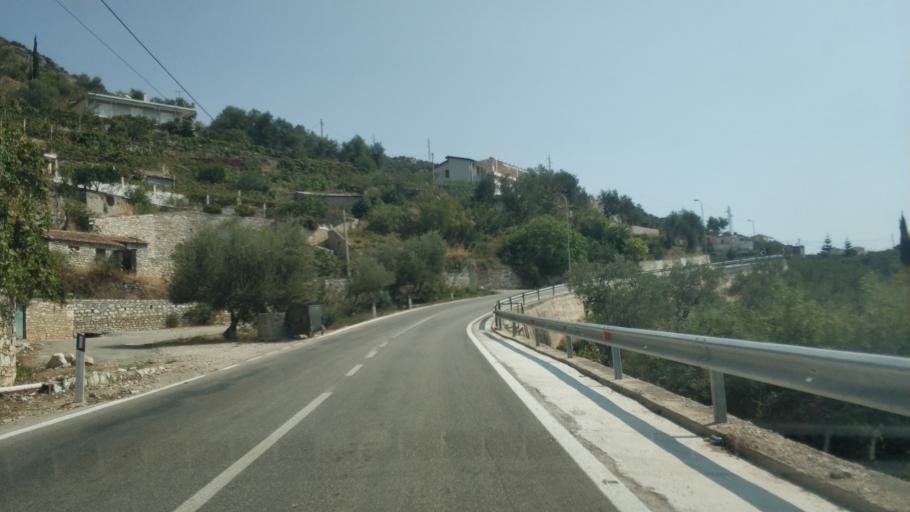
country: AL
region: Vlore
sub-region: Rrethi i Vlores
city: Himare
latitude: 40.0556
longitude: 19.8267
